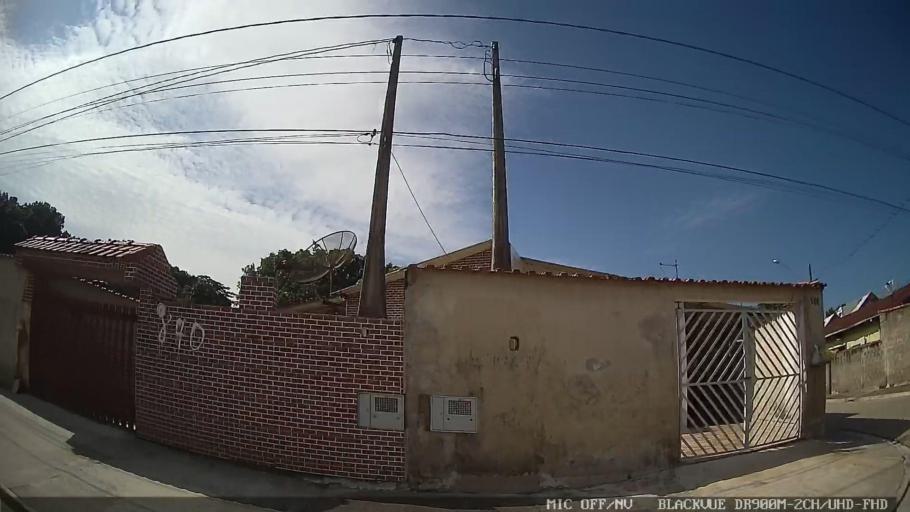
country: BR
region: Sao Paulo
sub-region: Itanhaem
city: Itanhaem
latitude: -24.1523
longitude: -46.7444
